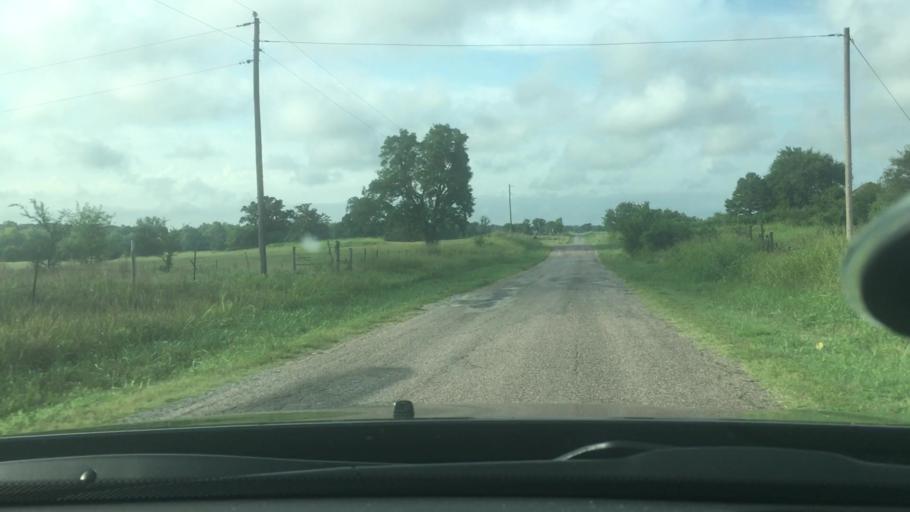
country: US
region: Oklahoma
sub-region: Pontotoc County
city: Ada
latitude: 34.6896
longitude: -96.5298
